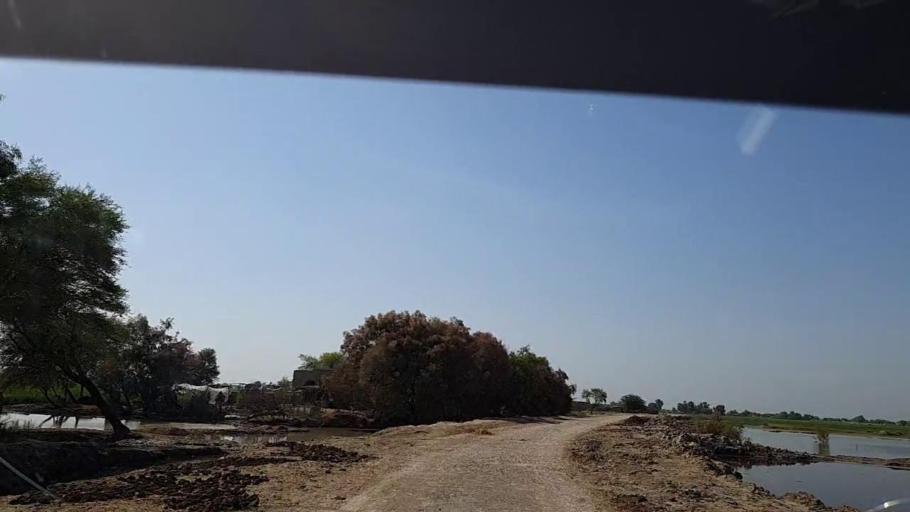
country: PK
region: Sindh
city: Tangwani
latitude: 28.3281
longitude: 69.0784
